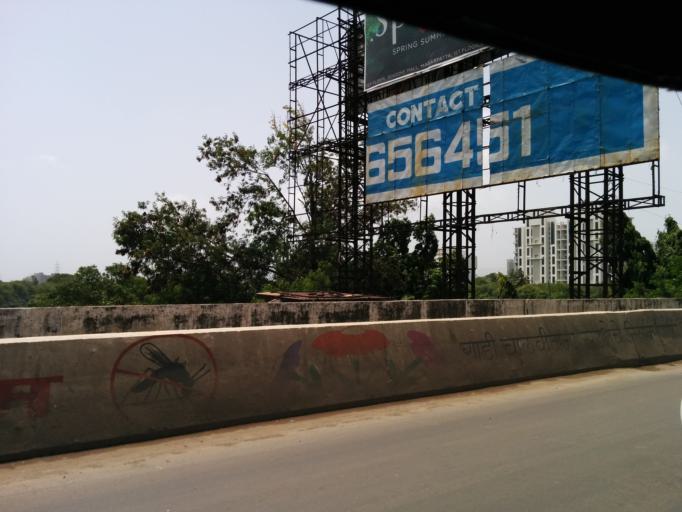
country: IN
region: Maharashtra
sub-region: Pune Division
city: Lohogaon
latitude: 18.5263
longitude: 73.9322
